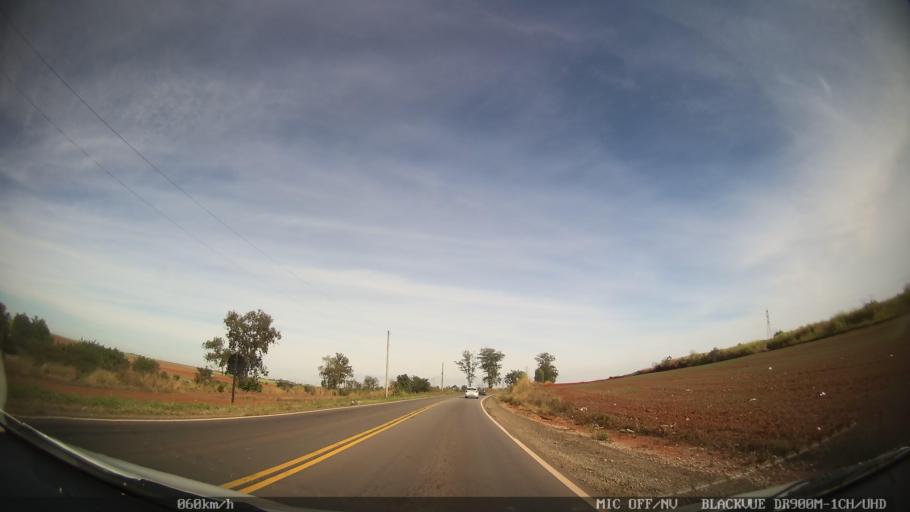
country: BR
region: Sao Paulo
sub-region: Rio Das Pedras
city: Rio das Pedras
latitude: -22.7892
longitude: -47.6364
